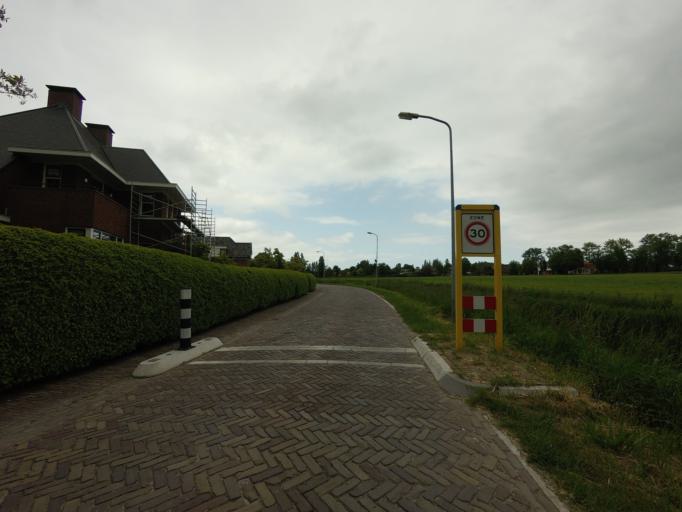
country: NL
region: North Holland
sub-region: Gemeente Hoorn
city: Hoorn
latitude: 52.6766
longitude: 5.0263
